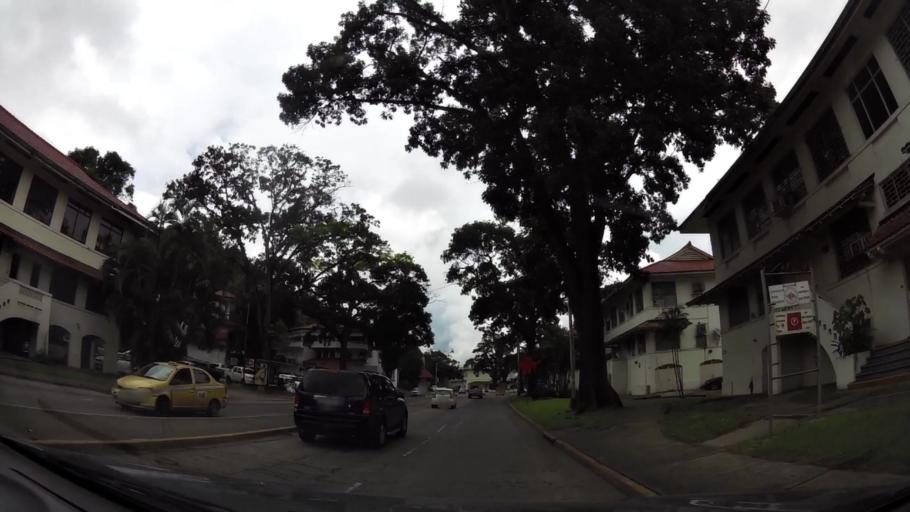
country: PA
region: Panama
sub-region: Distrito de Panama
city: Ancon
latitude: 8.9542
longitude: -79.5571
